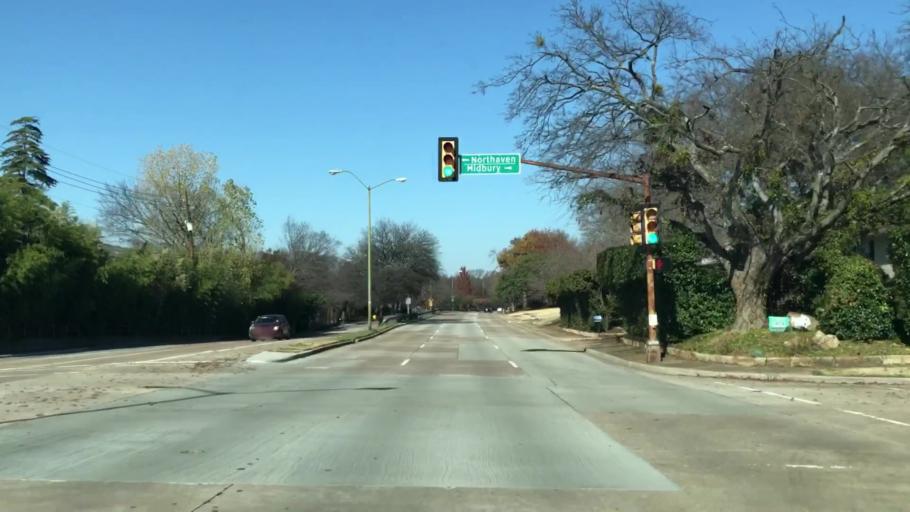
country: US
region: Texas
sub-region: Dallas County
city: University Park
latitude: 32.9014
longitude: -96.7882
